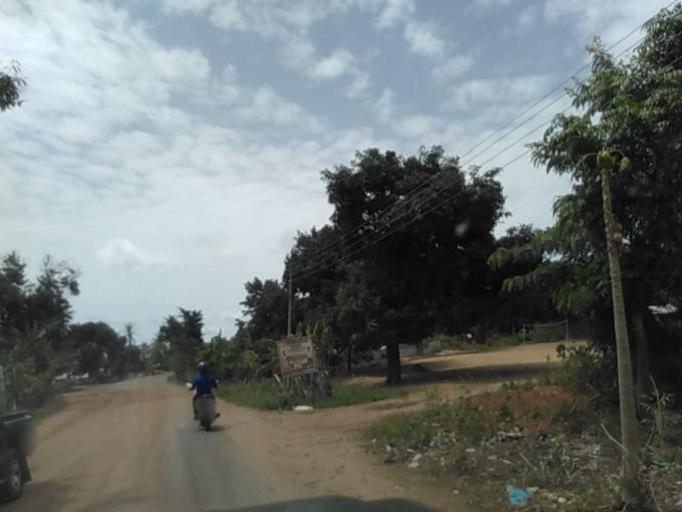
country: GH
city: Akropong
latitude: 6.0964
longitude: 0.1645
